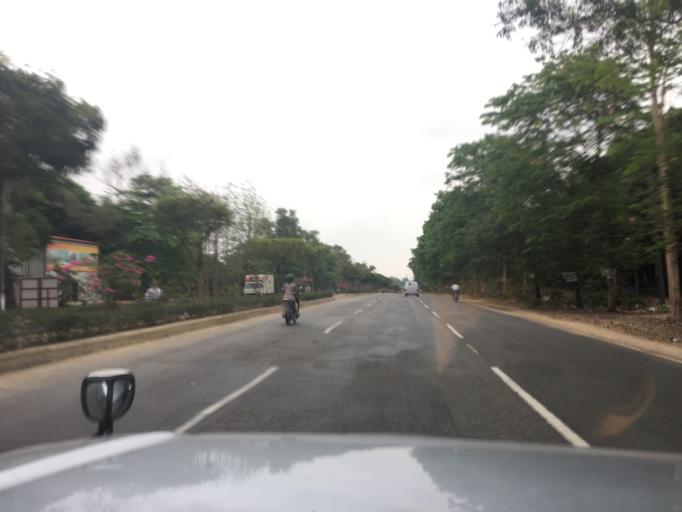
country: MM
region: Bago
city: Bago
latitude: 17.2416
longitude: 96.4641
